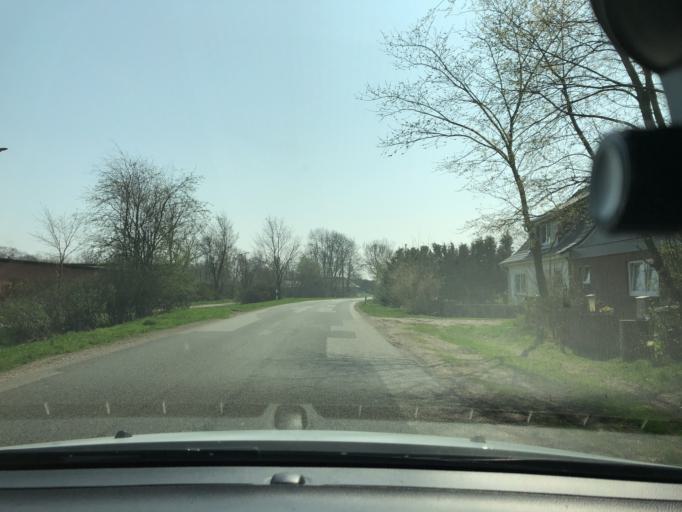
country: DE
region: Schleswig-Holstein
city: Grossenwiehe
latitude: 54.6908
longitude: 9.2399
